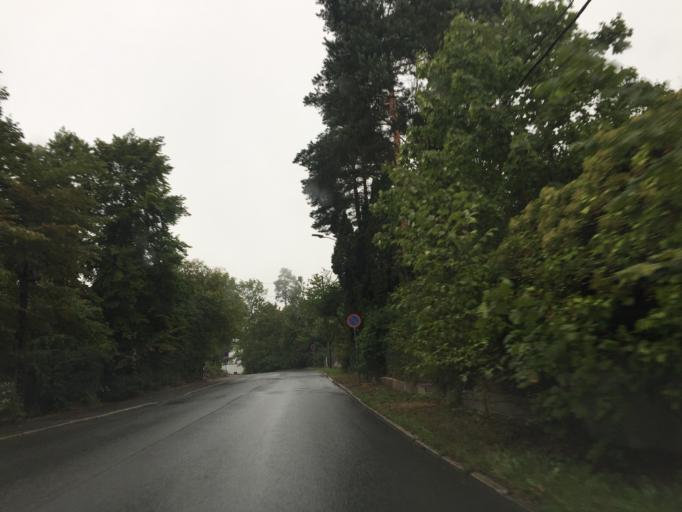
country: NO
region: Oslo
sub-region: Oslo
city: Sjolyststranda
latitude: 59.9544
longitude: 10.6910
